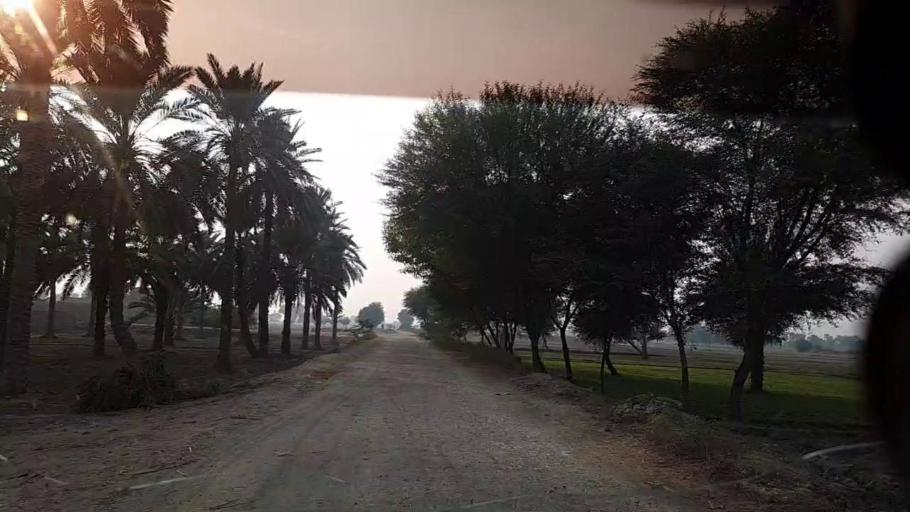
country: PK
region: Sindh
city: Kot Diji
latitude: 27.4373
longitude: 68.6262
